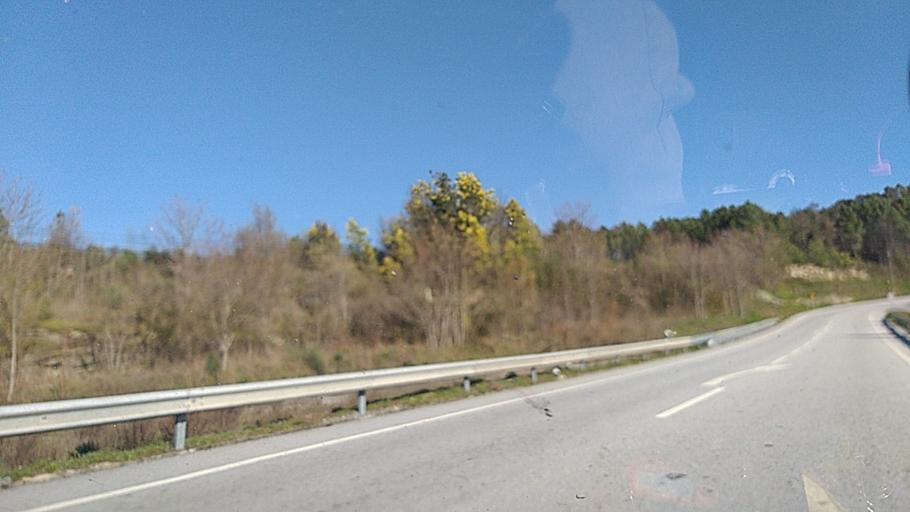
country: PT
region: Guarda
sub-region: Fornos de Algodres
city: Fornos de Algodres
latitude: 40.6199
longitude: -7.5115
